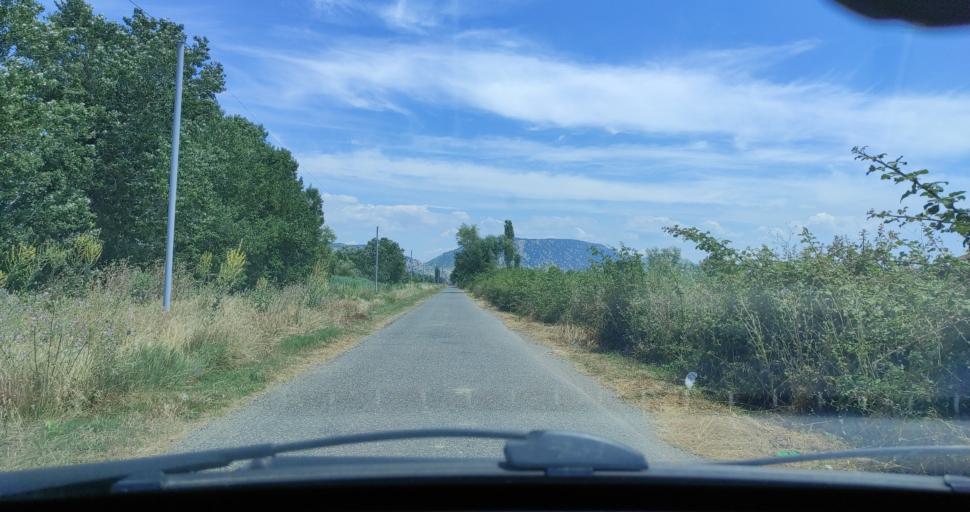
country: AL
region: Shkoder
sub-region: Rrethi i Shkodres
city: Velipoje
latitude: 41.8787
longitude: 19.3897
